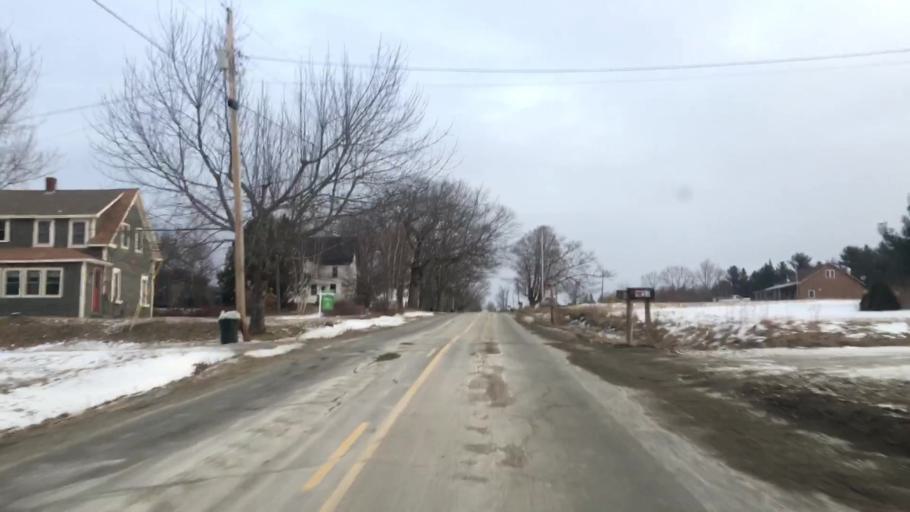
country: US
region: Maine
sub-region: Hancock County
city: Franklin
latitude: 44.7070
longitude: -68.3401
